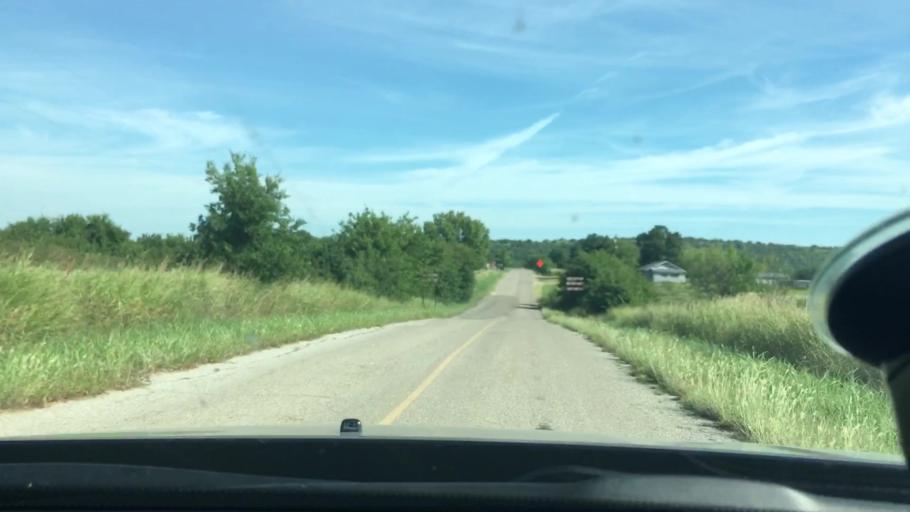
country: US
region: Oklahoma
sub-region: Carter County
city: Lone Grove
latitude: 34.3288
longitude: -97.2825
